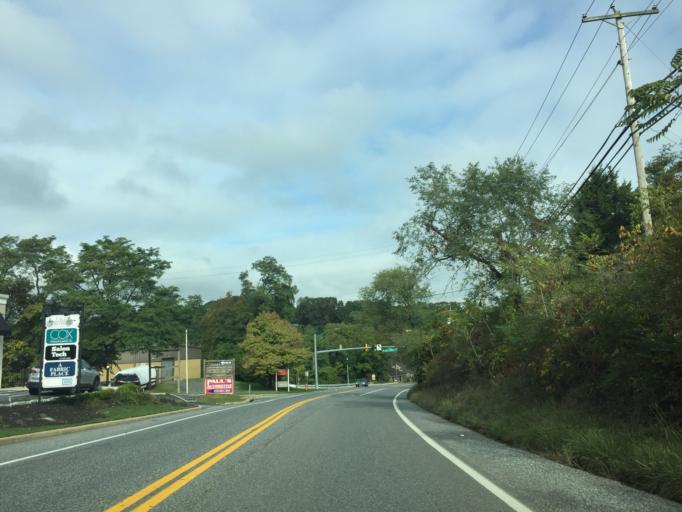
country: US
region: Maryland
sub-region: Baltimore County
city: Lutherville
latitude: 39.3847
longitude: -76.6584
